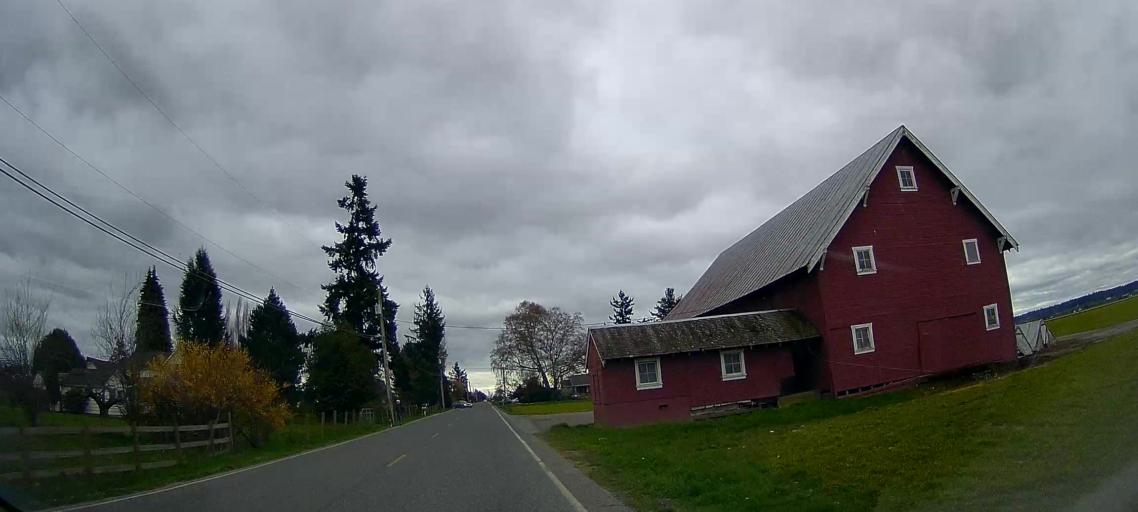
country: US
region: Washington
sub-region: Skagit County
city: Mount Vernon
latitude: 48.4048
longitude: -122.4010
